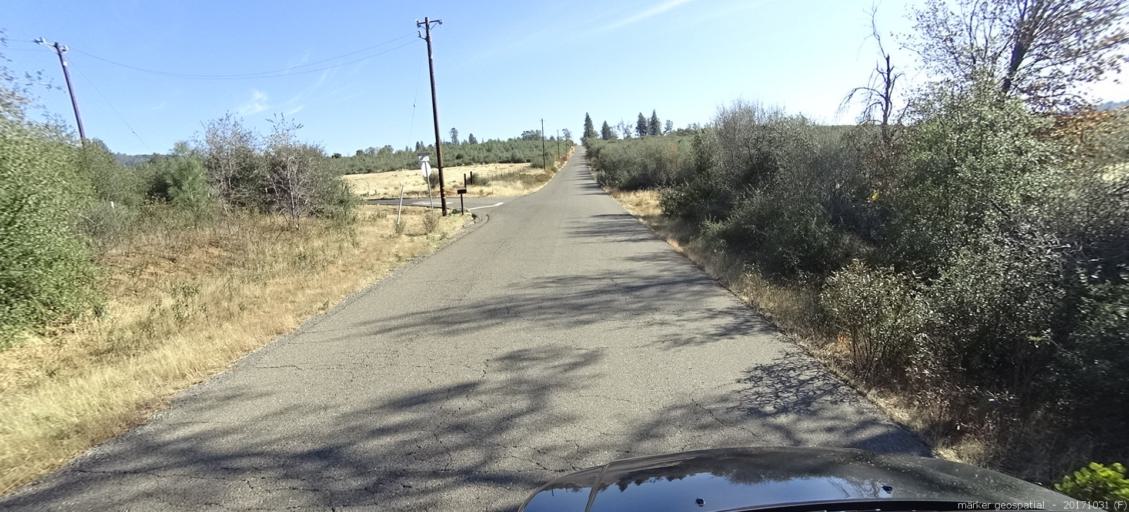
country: US
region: California
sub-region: Shasta County
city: Shingletown
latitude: 40.4463
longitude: -121.8648
